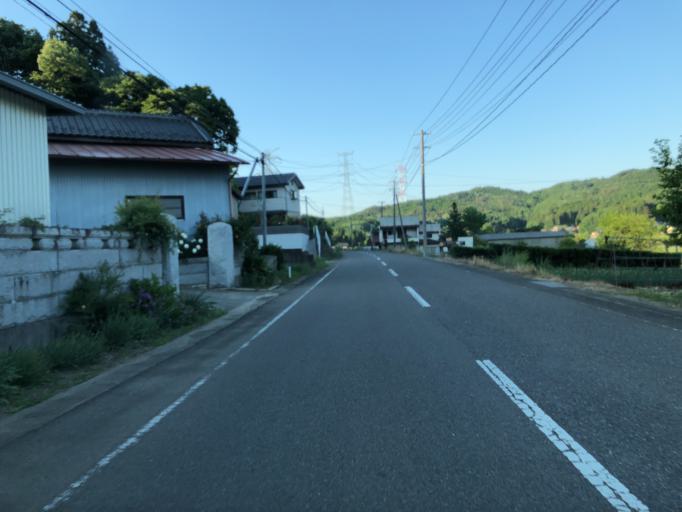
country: JP
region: Fukushima
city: Ishikawa
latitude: 37.0659
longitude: 140.4218
